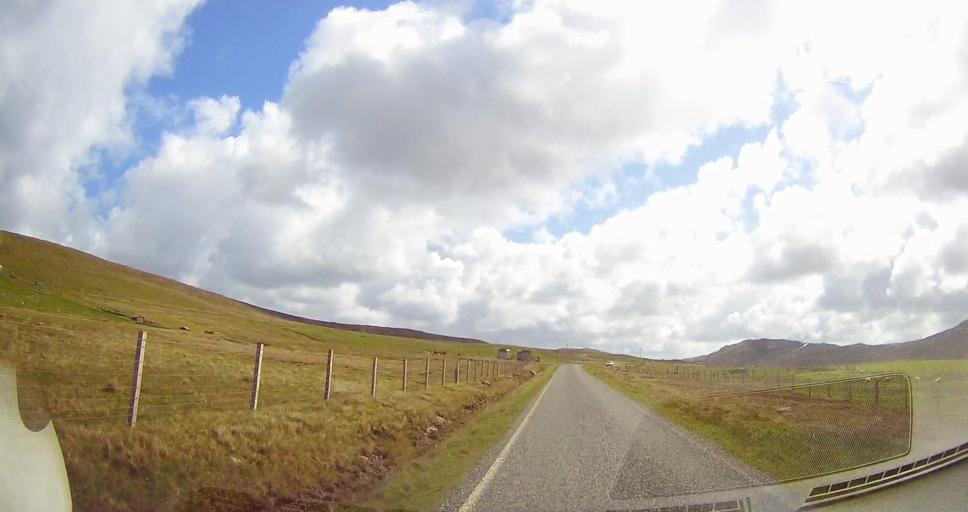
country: GB
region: Scotland
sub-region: Shetland Islands
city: Lerwick
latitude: 60.5679
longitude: -1.3330
